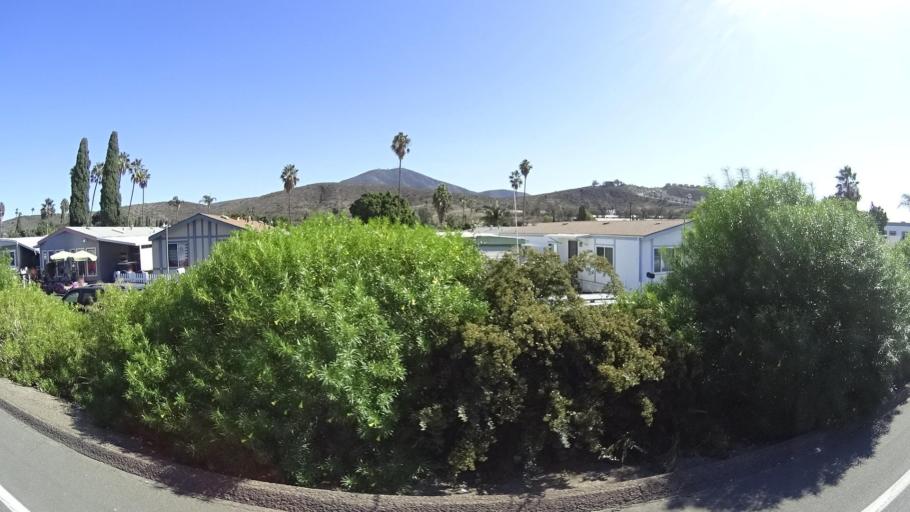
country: US
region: California
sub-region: San Diego County
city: Rancho San Diego
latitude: 32.7280
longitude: -116.9650
